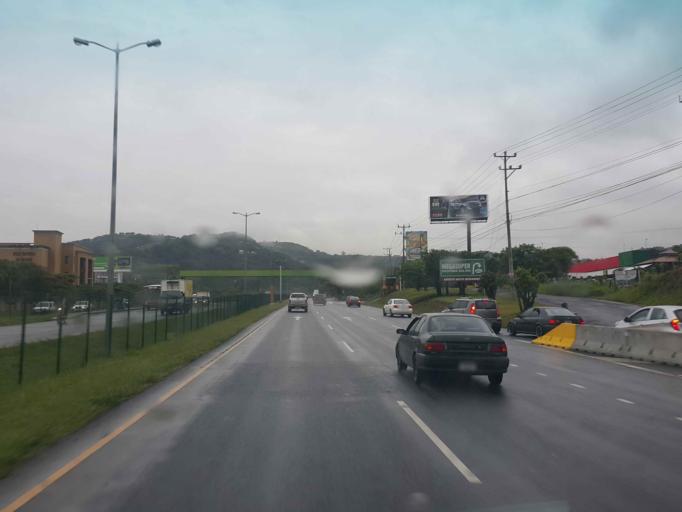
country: CR
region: San Jose
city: Santa Ana
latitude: 9.9433
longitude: -84.1938
